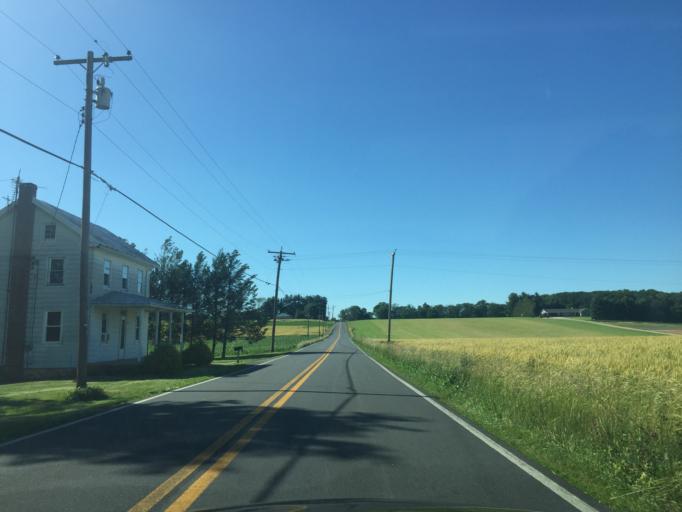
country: US
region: Maryland
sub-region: Carroll County
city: Westminster
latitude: 39.5923
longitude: -76.9325
